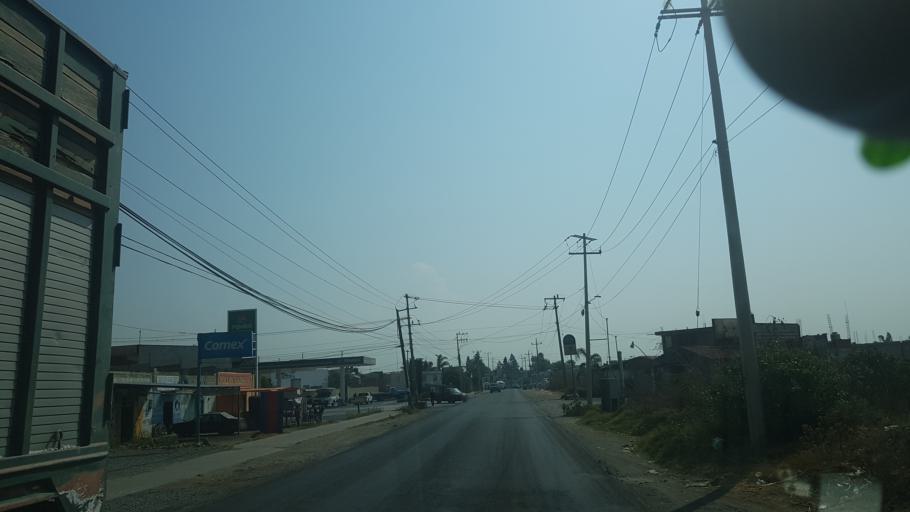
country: MX
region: Puebla
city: Cholula
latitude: 19.0578
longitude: -98.3209
